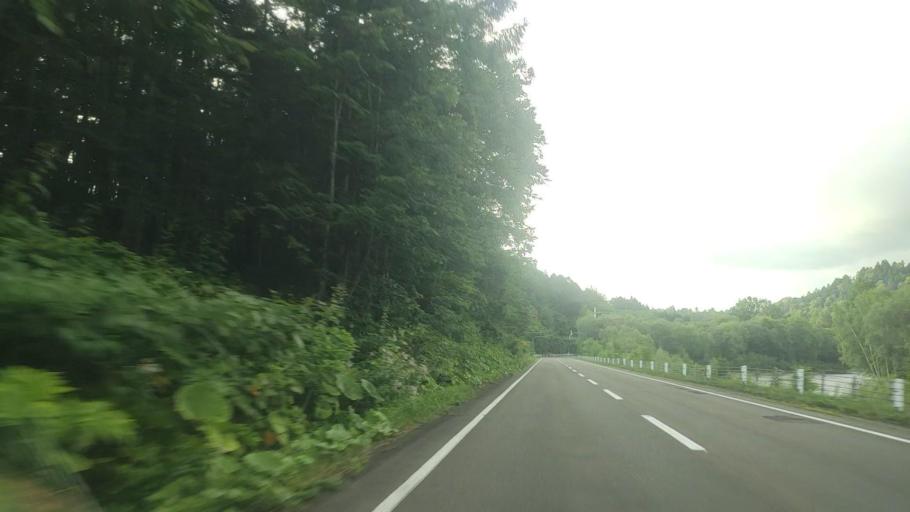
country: JP
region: Hokkaido
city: Bibai
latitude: 43.1240
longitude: 142.1027
